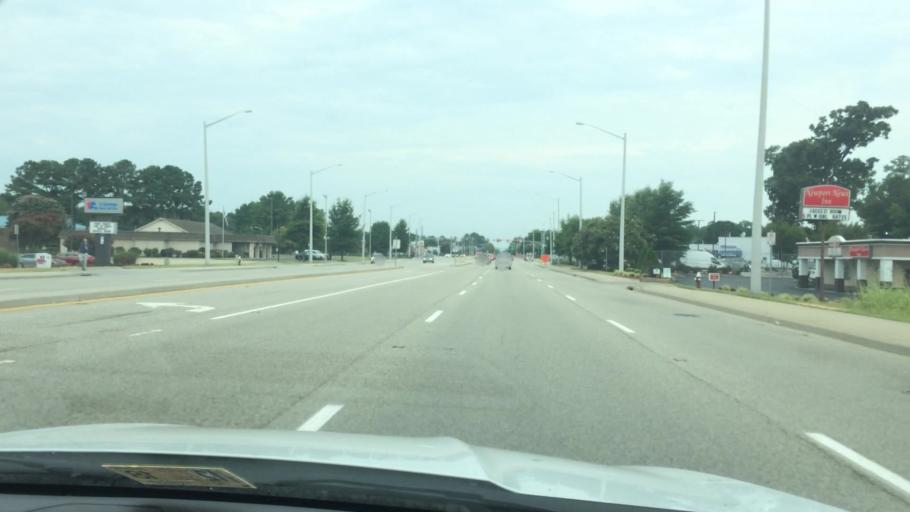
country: US
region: Virginia
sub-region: York County
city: Yorktown
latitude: 37.1465
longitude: -76.5261
